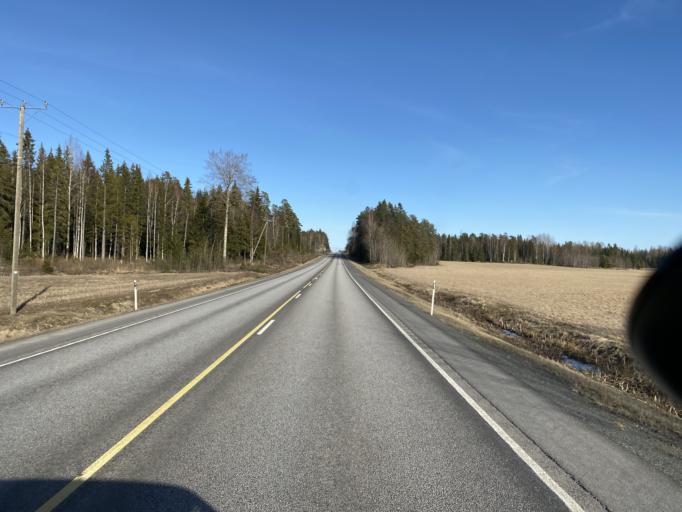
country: FI
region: Satakunta
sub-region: Rauma
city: Kiukainen
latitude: 61.1313
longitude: 22.0216
